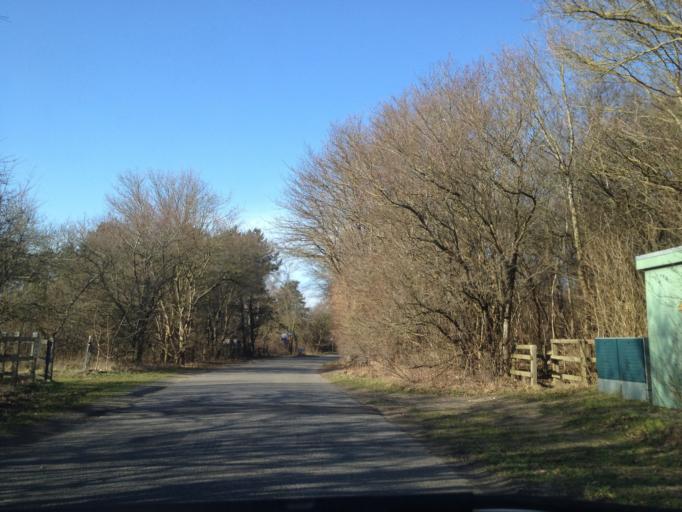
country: DK
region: South Denmark
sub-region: Kerteminde Kommune
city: Munkebo
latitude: 55.5536
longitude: 10.6169
